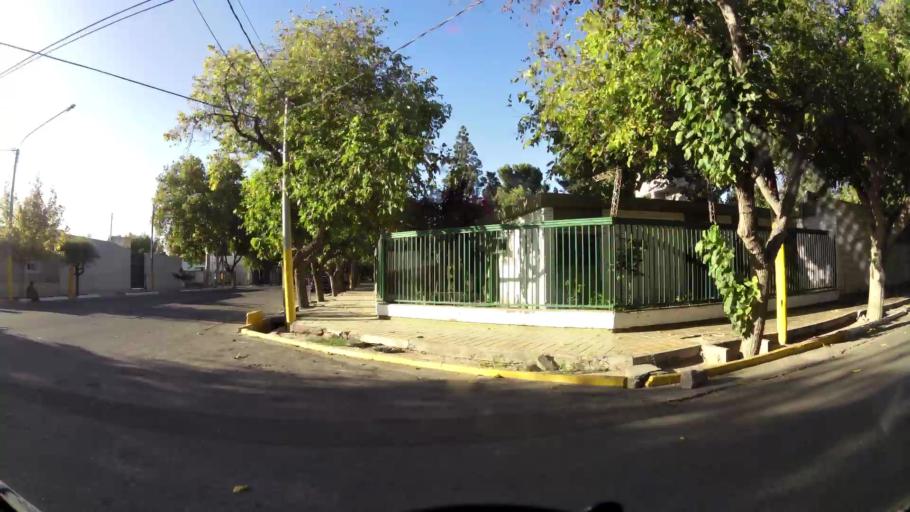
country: AR
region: San Juan
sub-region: Departamento de Santa Lucia
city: Santa Lucia
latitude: -31.5390
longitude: -68.5063
